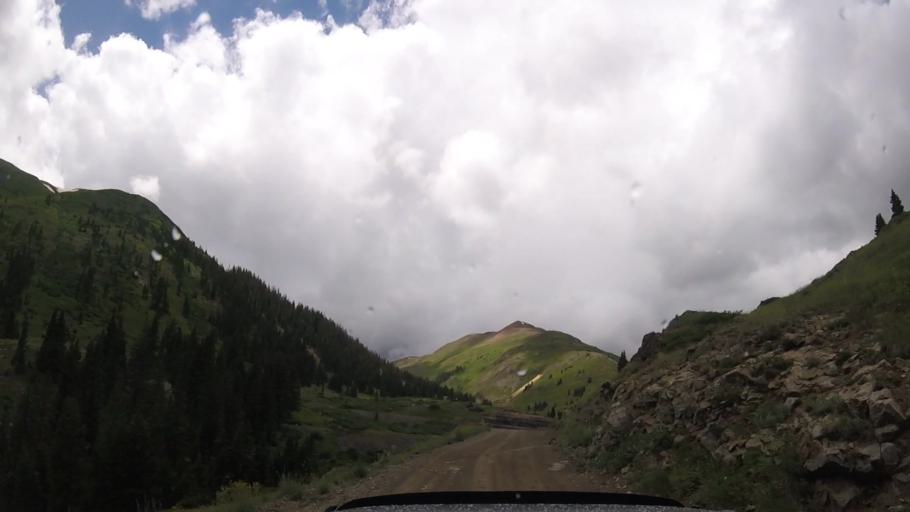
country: US
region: Colorado
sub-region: Ouray County
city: Ouray
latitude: 37.9288
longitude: -107.5660
